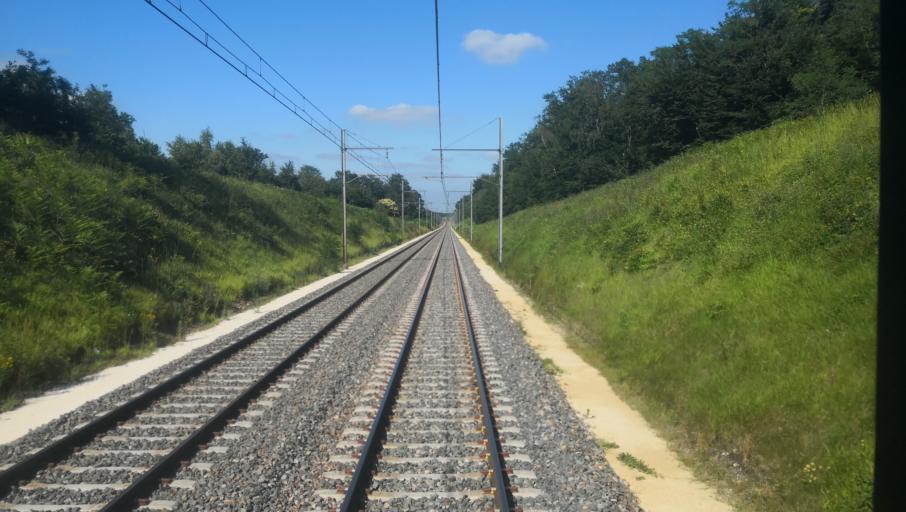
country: FR
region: Ile-de-France
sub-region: Departement de Seine-et-Marne
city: Veneux-les-Sablons
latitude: 48.3532
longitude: 2.7867
